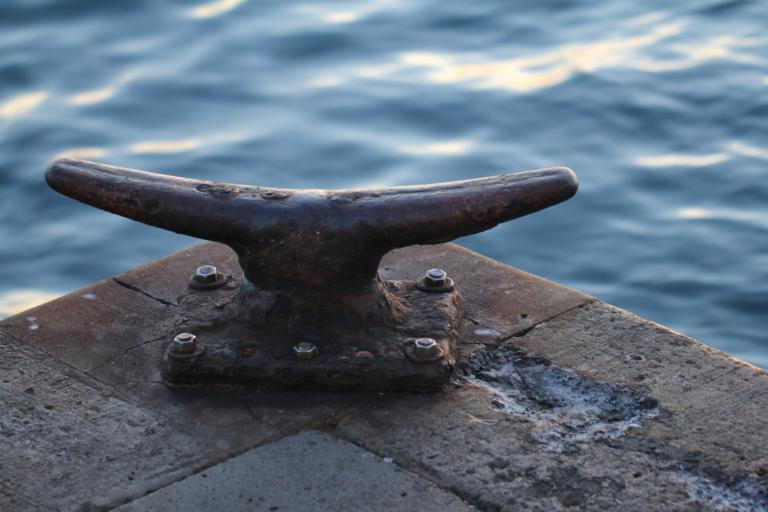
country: US
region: Hawaii
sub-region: Maui County
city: Lahaina
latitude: 20.8719
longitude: -156.6789
